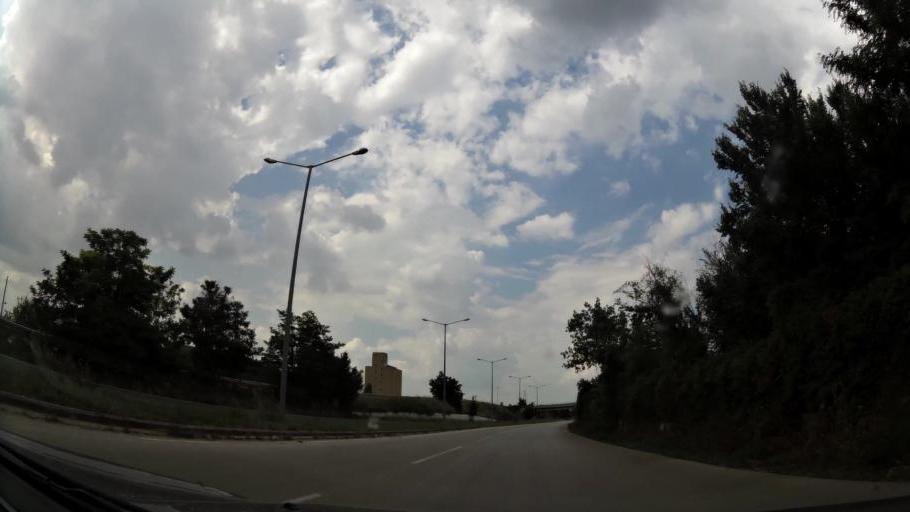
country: GR
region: West Macedonia
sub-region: Nomos Kozanis
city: Koila
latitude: 40.3403
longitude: 21.8245
